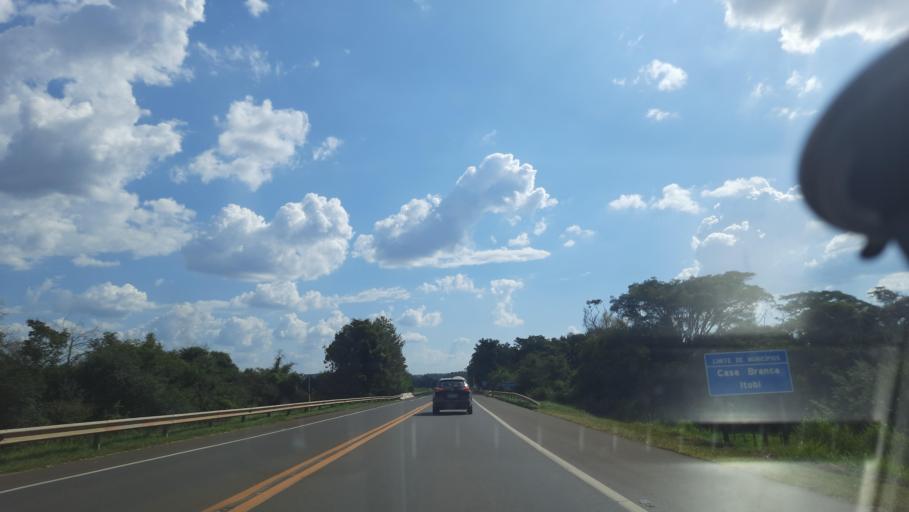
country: BR
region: Sao Paulo
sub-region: Casa Branca
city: Casa Branca
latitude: -21.7435
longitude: -46.9826
